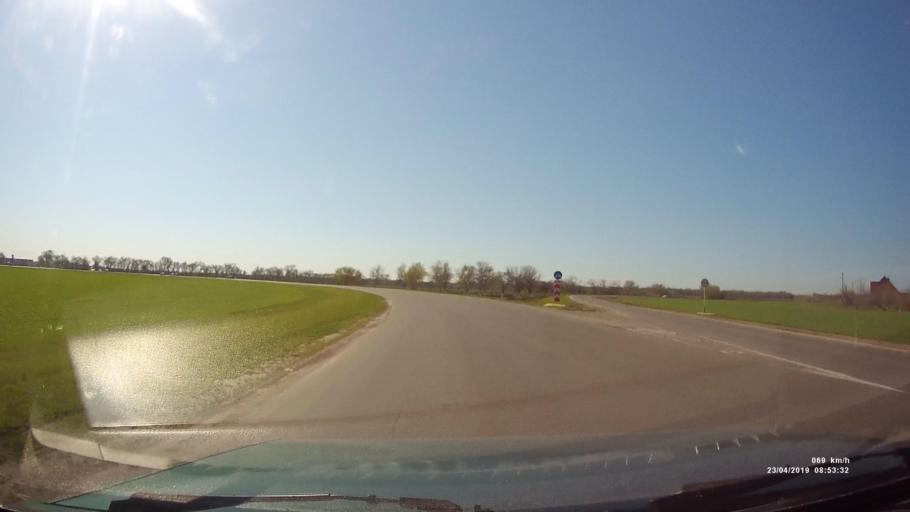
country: RU
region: Rostov
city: Sal'sk
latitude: 46.4750
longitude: 41.4747
